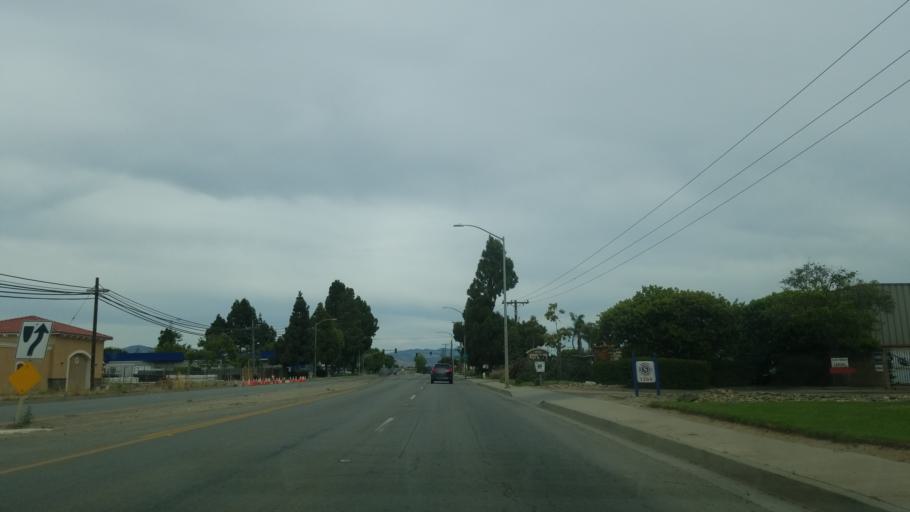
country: US
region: California
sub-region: Santa Barbara County
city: Santa Maria
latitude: 34.9206
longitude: -120.4567
